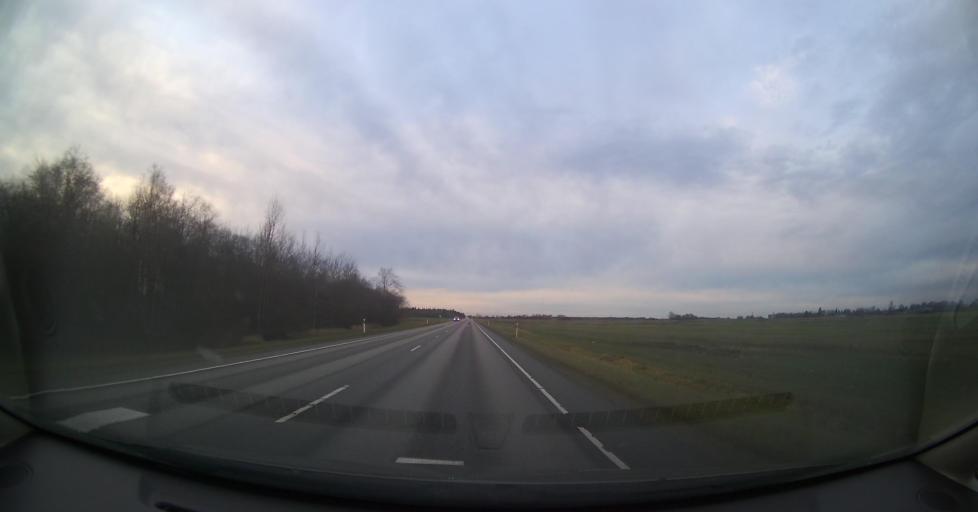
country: EE
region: Ida-Virumaa
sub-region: Kohtla-Jaerve linn
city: Kohtla-Jarve
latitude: 59.4207
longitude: 27.2401
